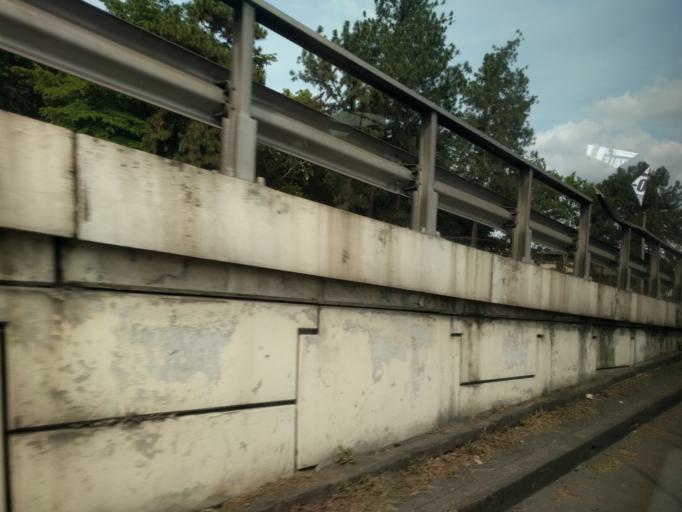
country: PA
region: Panama
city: Panama
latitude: 8.9782
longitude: -79.5367
